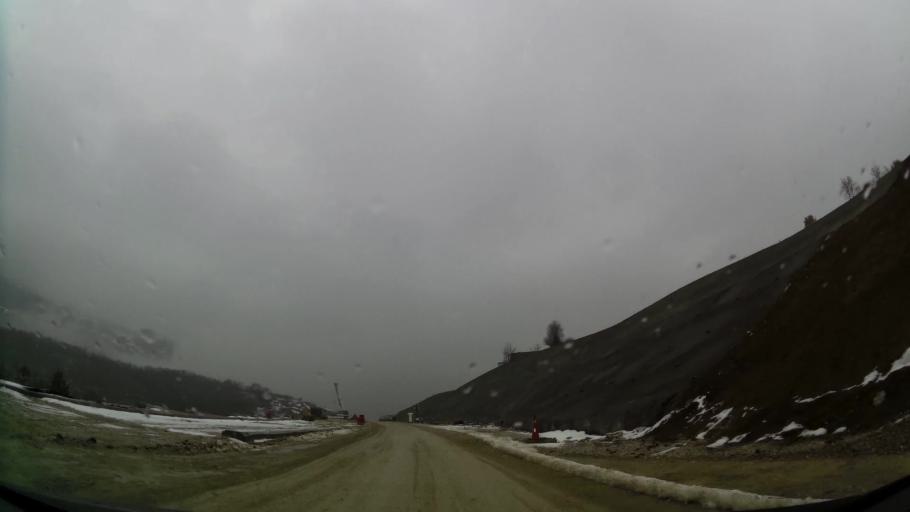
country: XK
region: Ferizaj
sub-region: Hani i Elezit
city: Hani i Elezit
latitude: 42.1656
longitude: 21.2837
